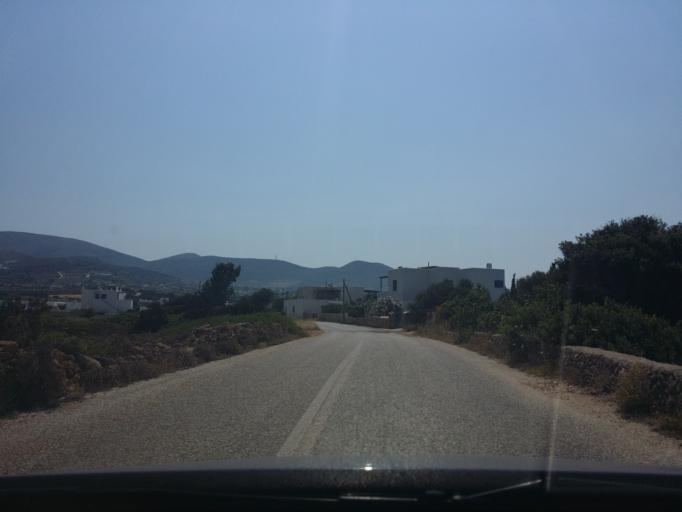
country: GR
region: South Aegean
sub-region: Nomos Kykladon
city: Antiparos
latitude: 37.0027
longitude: 25.1284
